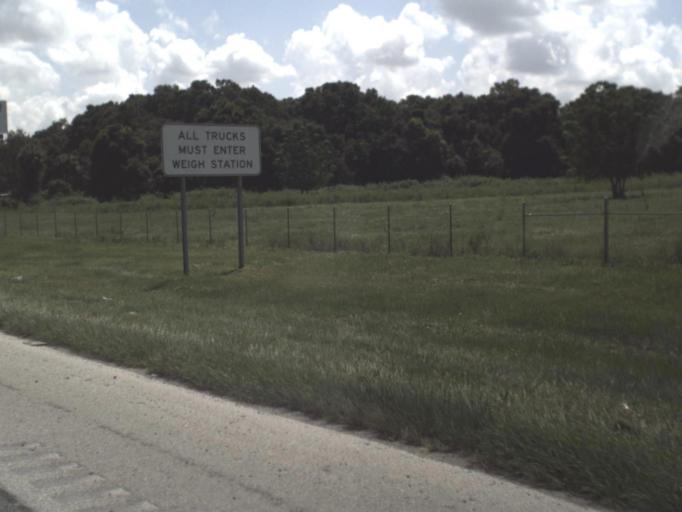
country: US
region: Florida
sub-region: Hillsborough County
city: Seffner
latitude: 28.0083
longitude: -82.2897
